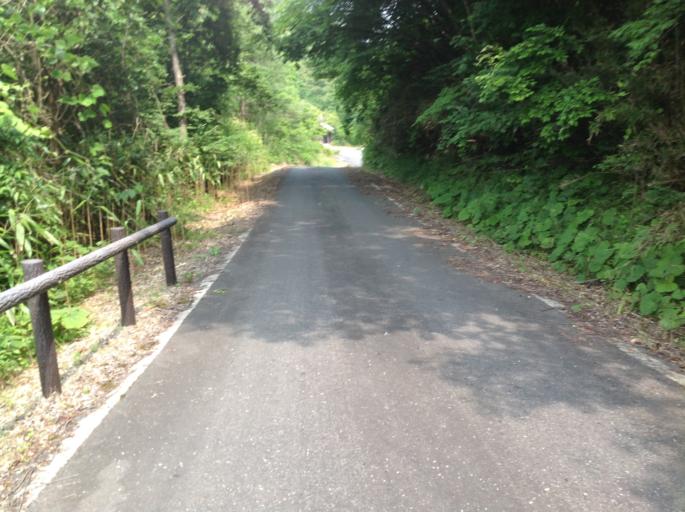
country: JP
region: Iwate
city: Ichinoseki
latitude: 38.8539
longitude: 141.2323
